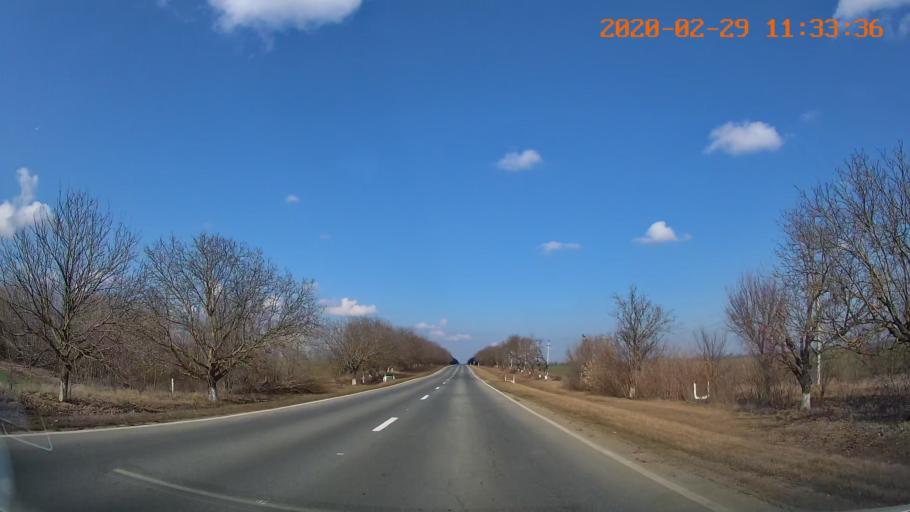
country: MD
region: Rezina
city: Saharna
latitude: 47.5538
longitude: 29.0827
